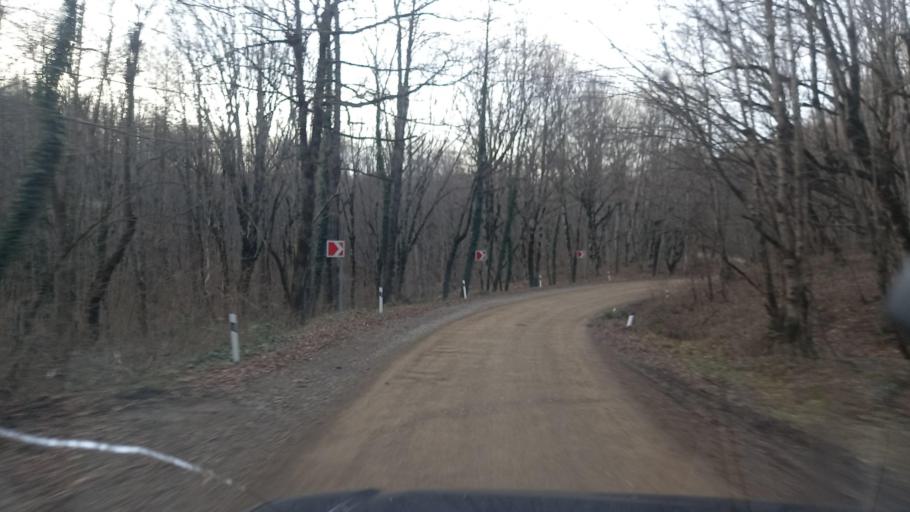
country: RU
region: Krasnodarskiy
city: Agoy
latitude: 44.3425
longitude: 39.2448
